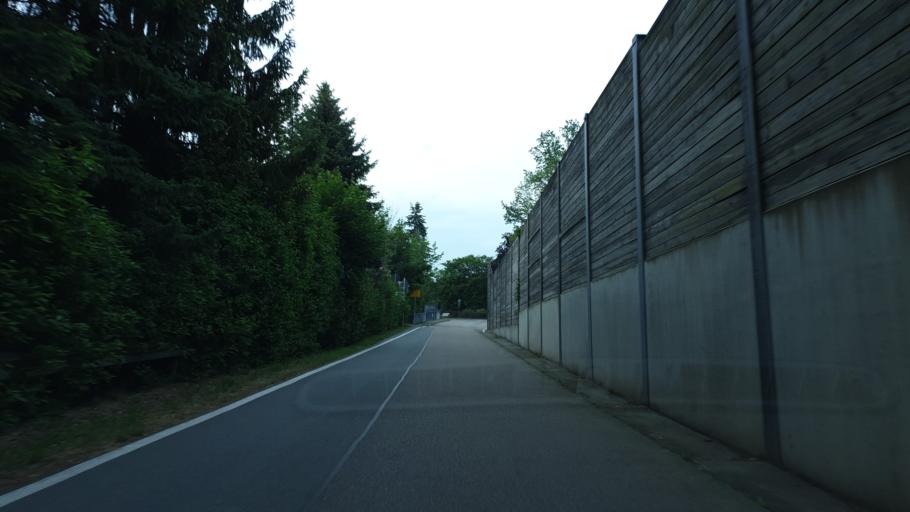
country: DE
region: Saxony
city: Oberlungwitz
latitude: 50.7938
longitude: 12.6905
